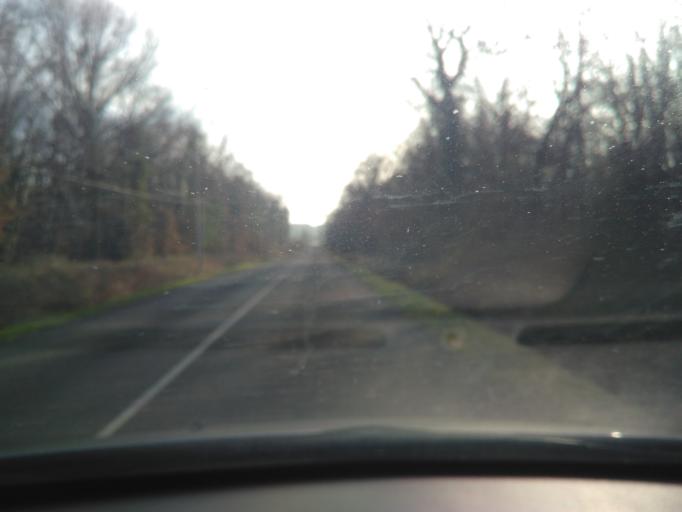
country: FR
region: Bourgogne
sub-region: Departement de la Nievre
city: Dornes
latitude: 46.7846
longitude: 3.2764
